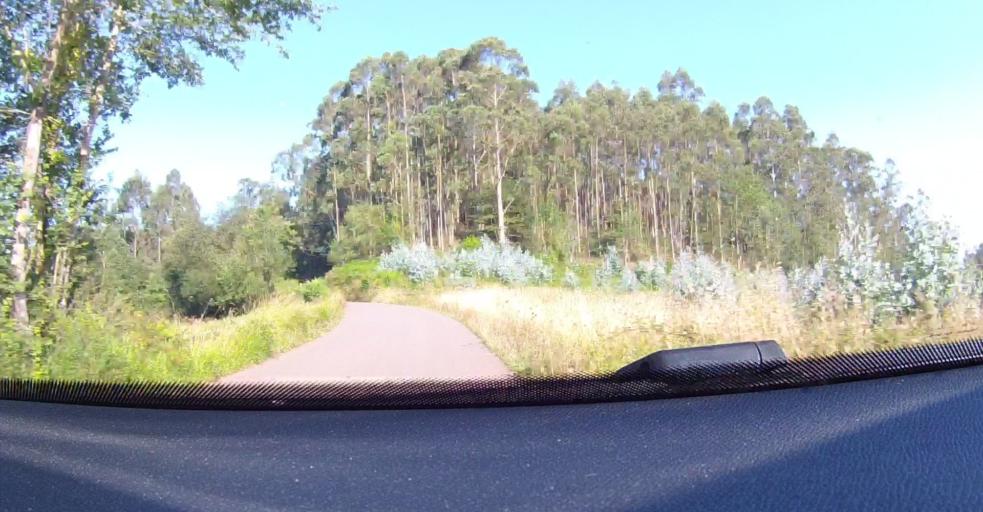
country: ES
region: Asturias
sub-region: Province of Asturias
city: Villaviciosa
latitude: 43.4859
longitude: -5.4017
